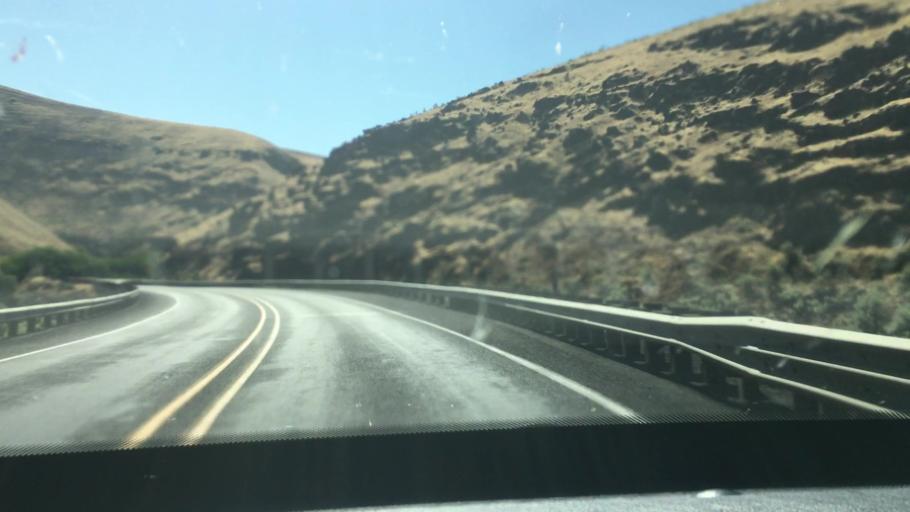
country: US
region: Washington
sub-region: Klickitat County
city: Goldendale
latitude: 45.6480
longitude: -120.8033
